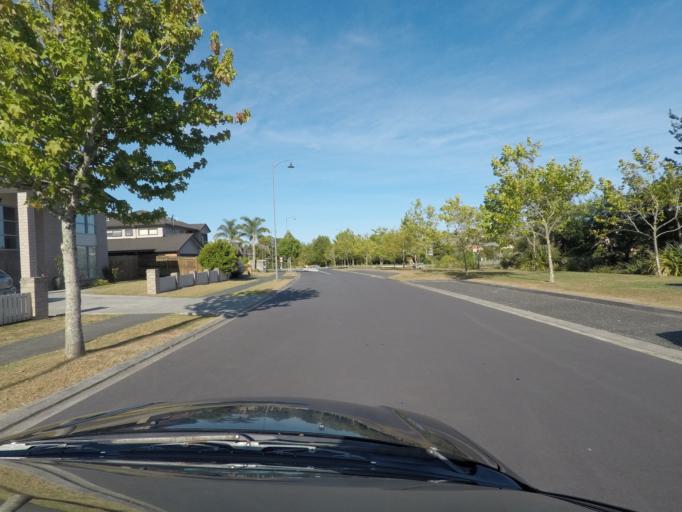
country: NZ
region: Auckland
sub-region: Auckland
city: Waitakere
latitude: -36.8832
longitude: 174.6037
